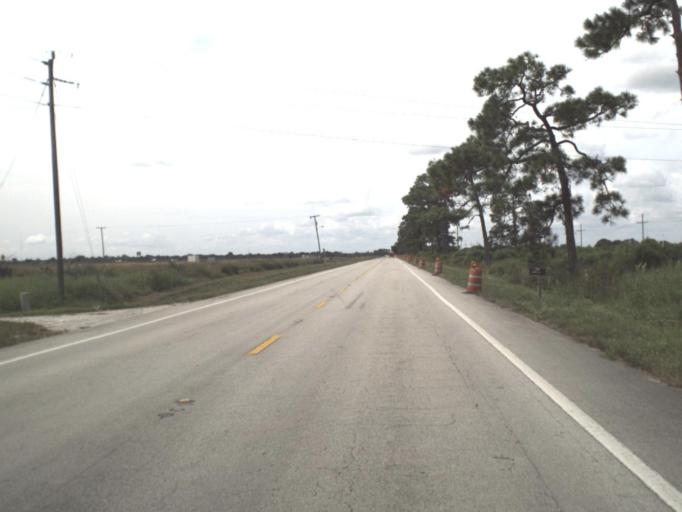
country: US
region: Florida
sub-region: Okeechobee County
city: Taylor Creek
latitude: 27.2727
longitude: -80.7255
